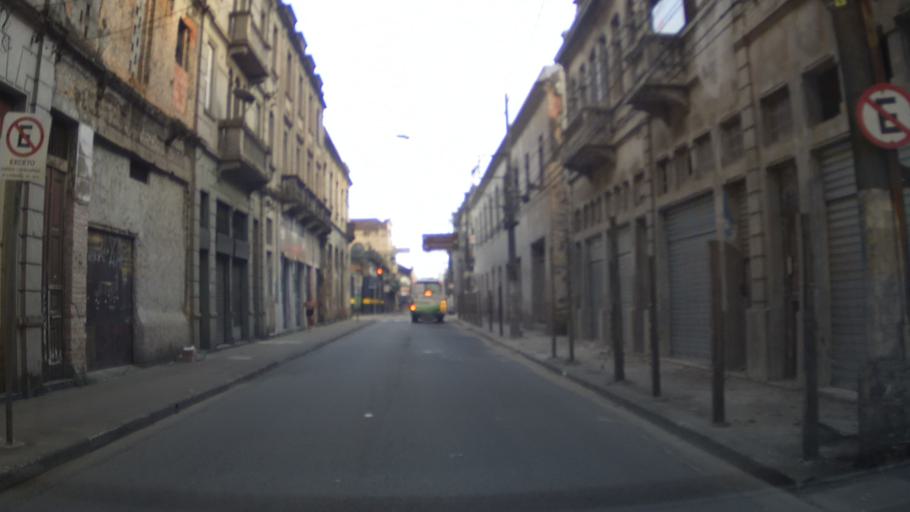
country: BR
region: Sao Paulo
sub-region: Santos
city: Santos
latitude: -23.9337
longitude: -46.3254
